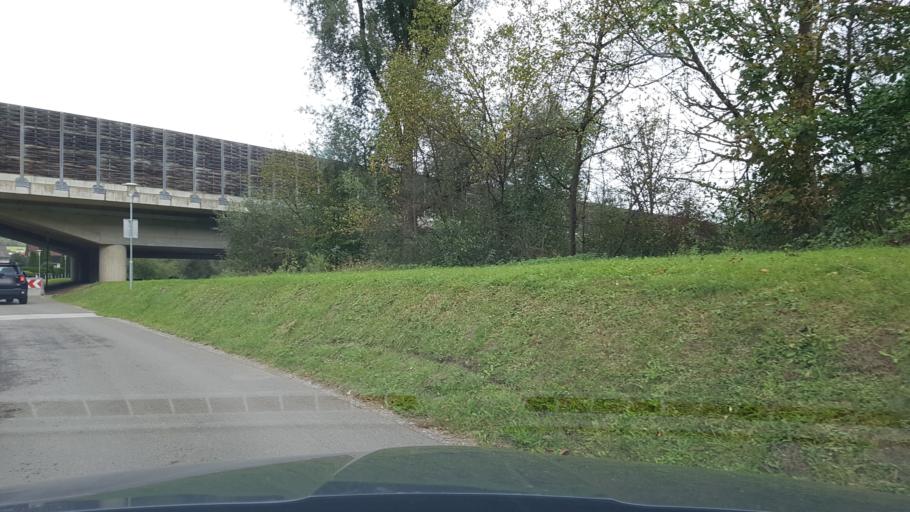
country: AT
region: Styria
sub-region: Politischer Bezirk Bruck-Muerzzuschlag
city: Sankt Marein im Muerztal
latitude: 47.4671
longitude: 15.3776
